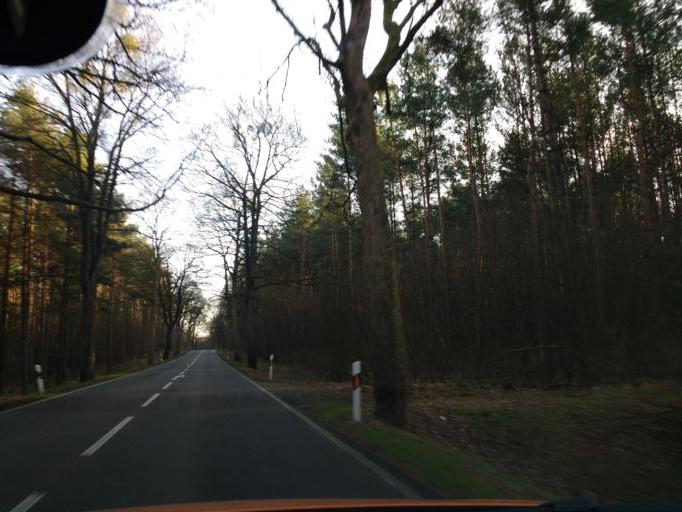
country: DE
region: Brandenburg
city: Werftpfuhl
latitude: 52.6604
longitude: 13.8696
